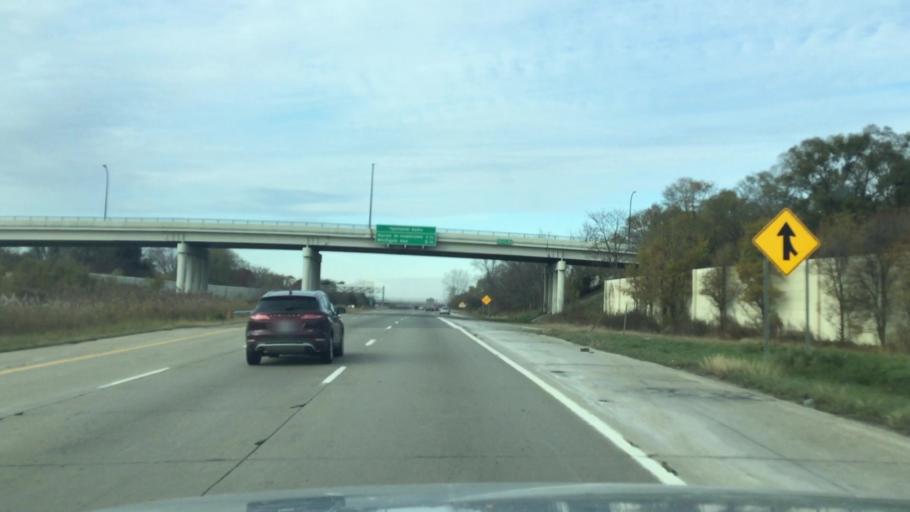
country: US
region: Michigan
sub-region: Washtenaw County
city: Ypsilanti
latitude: 42.2319
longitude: -83.5811
